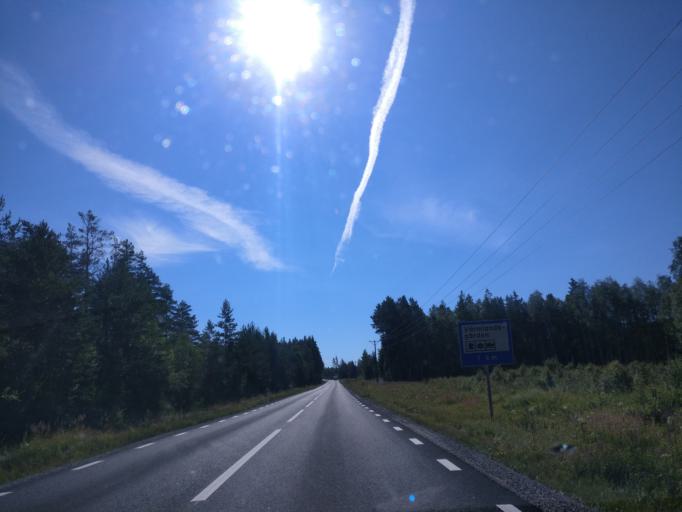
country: SE
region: Vaermland
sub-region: Hagfors Kommun
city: Hagfors
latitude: 60.0334
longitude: 13.8444
